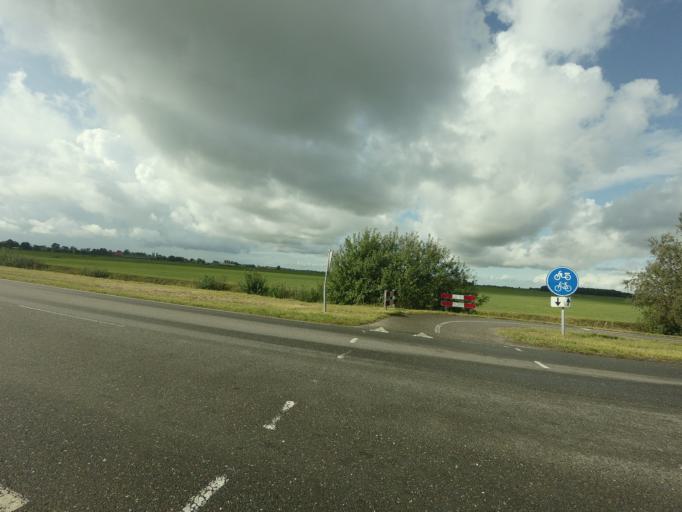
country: NL
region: Friesland
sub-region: Gemeente Tytsjerksteradiel
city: Garyp
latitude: 53.1580
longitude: 5.9508
